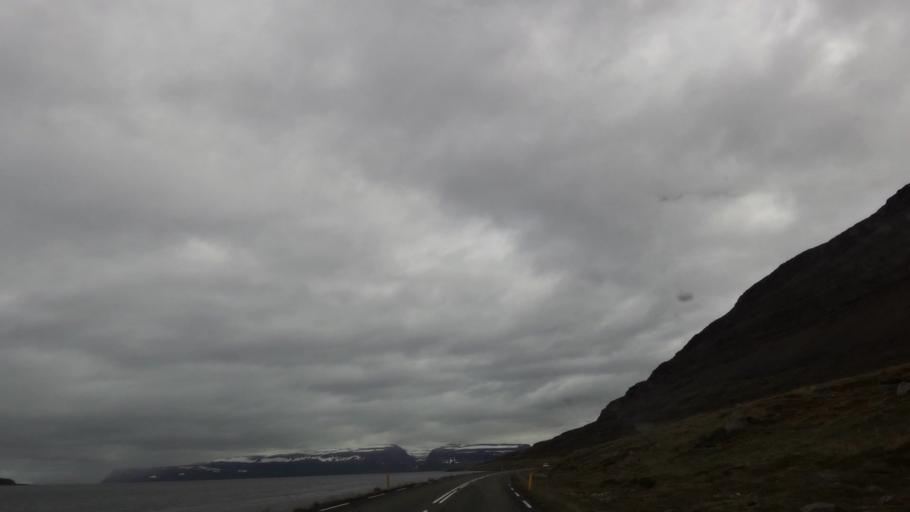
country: IS
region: Westfjords
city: Isafjoerdur
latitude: 66.0245
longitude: -22.7806
